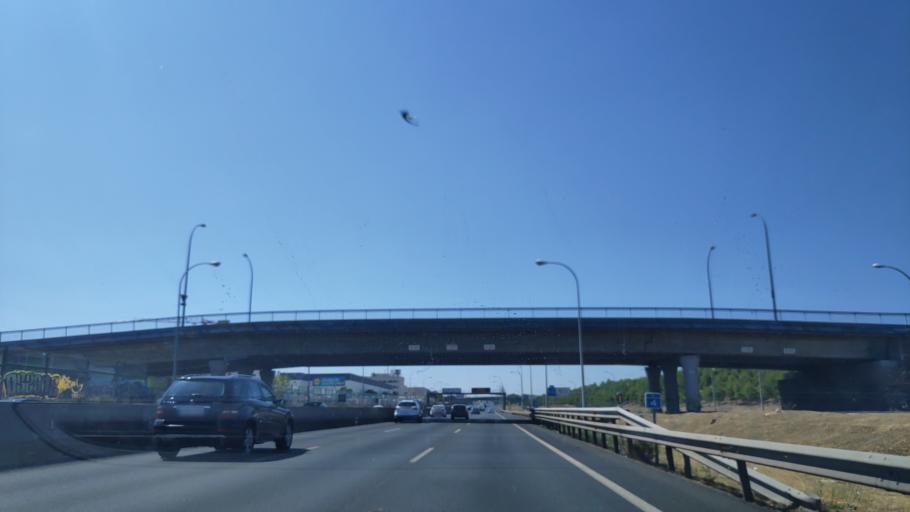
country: ES
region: Madrid
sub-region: Provincia de Madrid
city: Getafe
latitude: 40.3203
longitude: -3.7327
